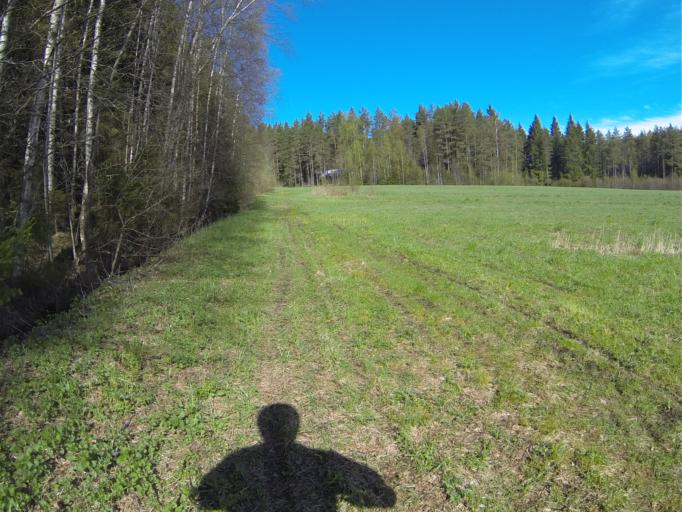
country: FI
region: Varsinais-Suomi
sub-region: Salo
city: Pertteli
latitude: 60.3945
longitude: 23.2149
